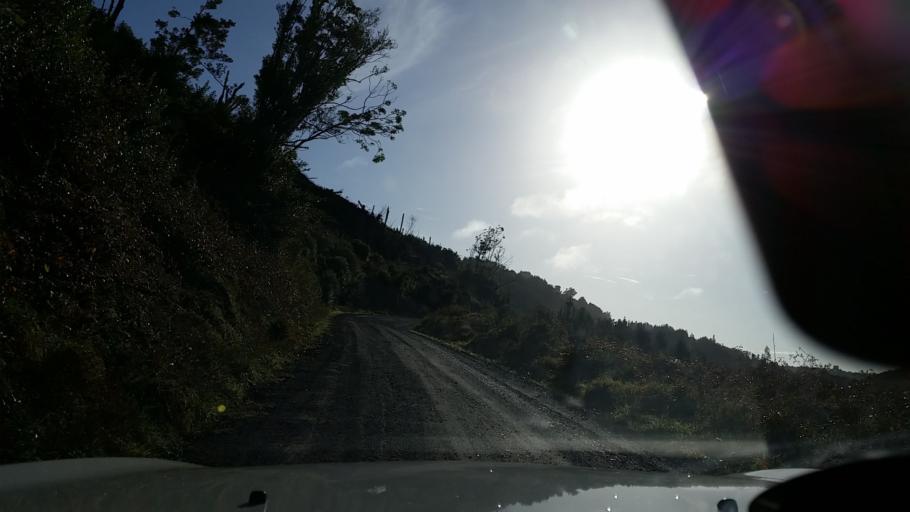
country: NZ
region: Bay of Plenty
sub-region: Kawerau District
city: Kawerau
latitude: -38.0361
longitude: 176.5510
